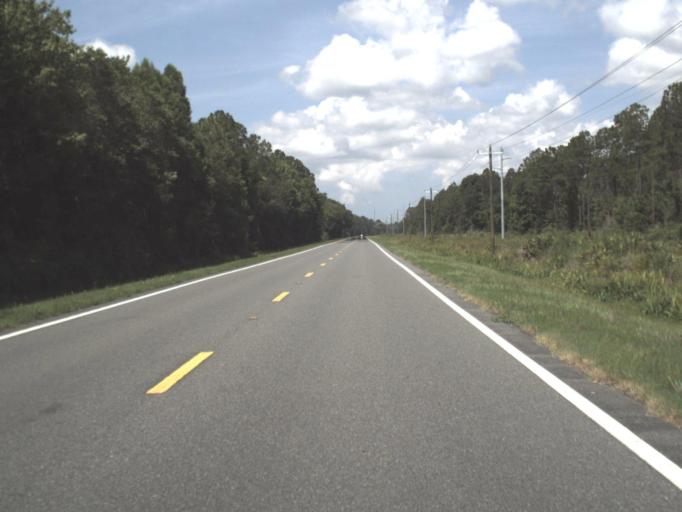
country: US
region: Florida
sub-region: Levy County
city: Chiefland
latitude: 29.2554
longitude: -82.8971
